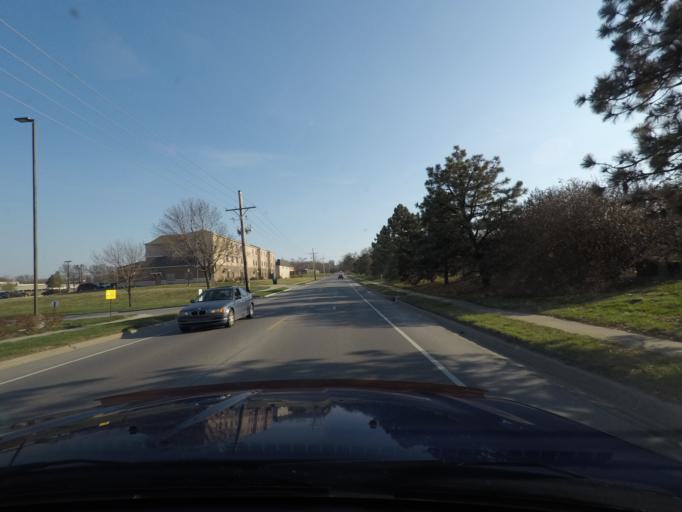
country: US
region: Kansas
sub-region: Douglas County
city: Lawrence
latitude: 38.9824
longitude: -95.2605
